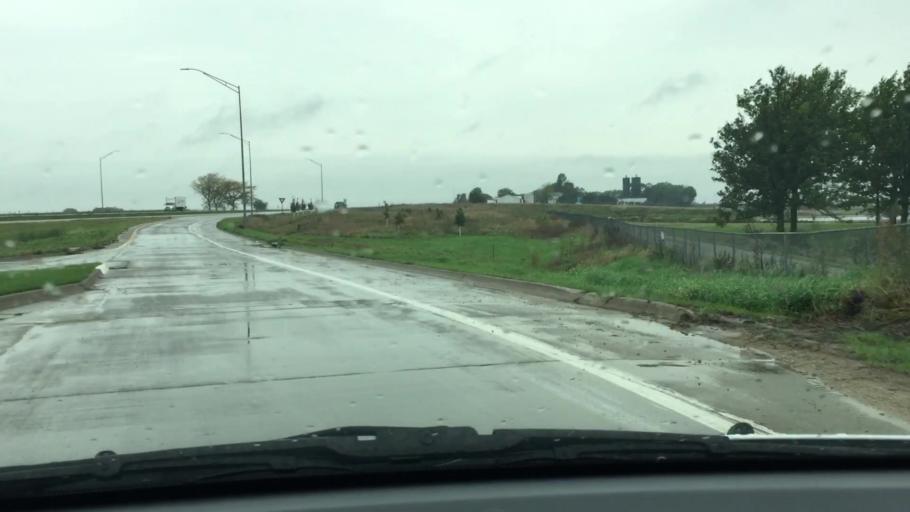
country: US
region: Iowa
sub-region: Iowa County
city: Marengo
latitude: 41.6965
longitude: -92.2330
